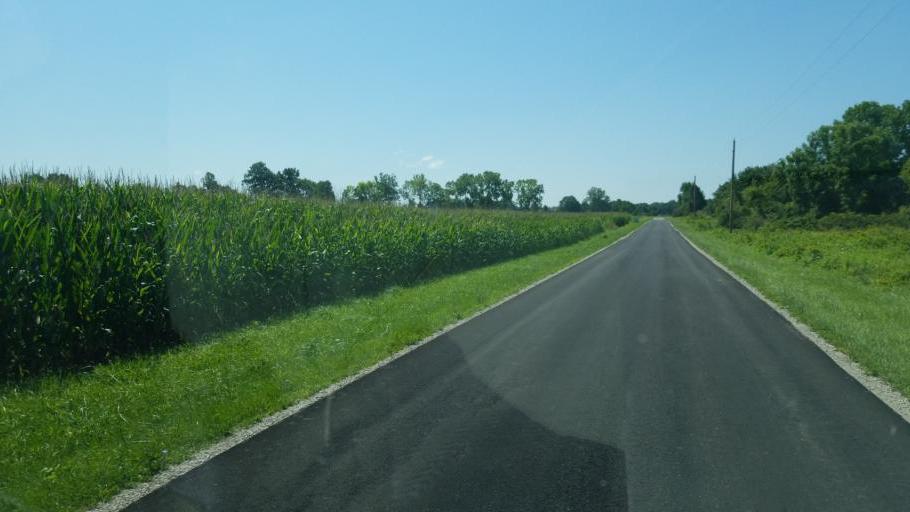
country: US
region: Ohio
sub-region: Delaware County
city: Ashley
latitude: 40.4328
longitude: -83.0396
